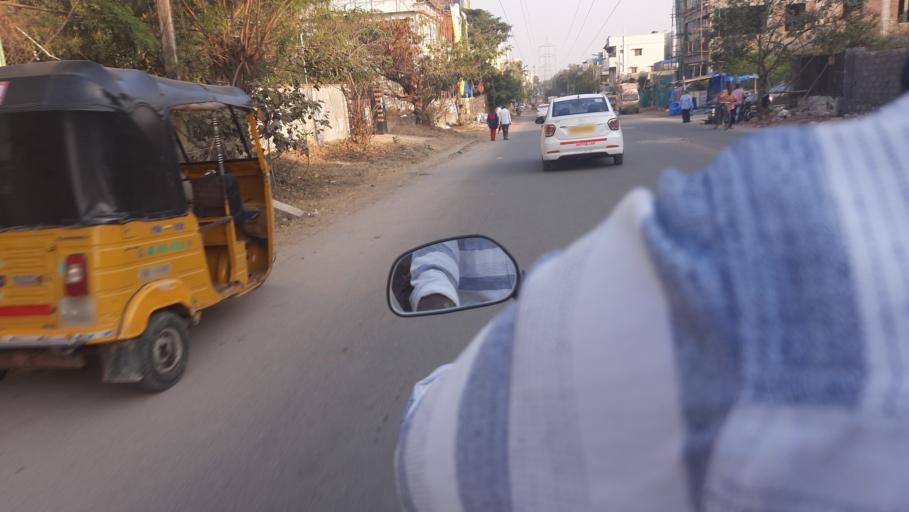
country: IN
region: Telangana
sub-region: Rangareddi
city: Secunderabad
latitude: 17.4907
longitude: 78.5490
